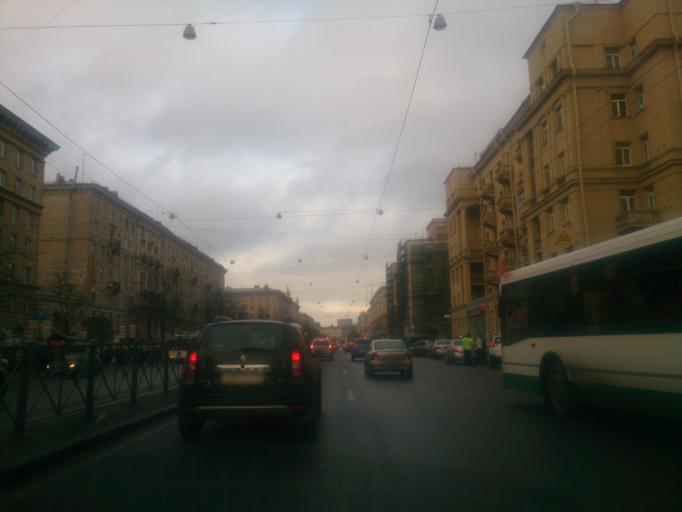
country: RU
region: St.-Petersburg
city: Avtovo
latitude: 59.8682
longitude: 30.2604
